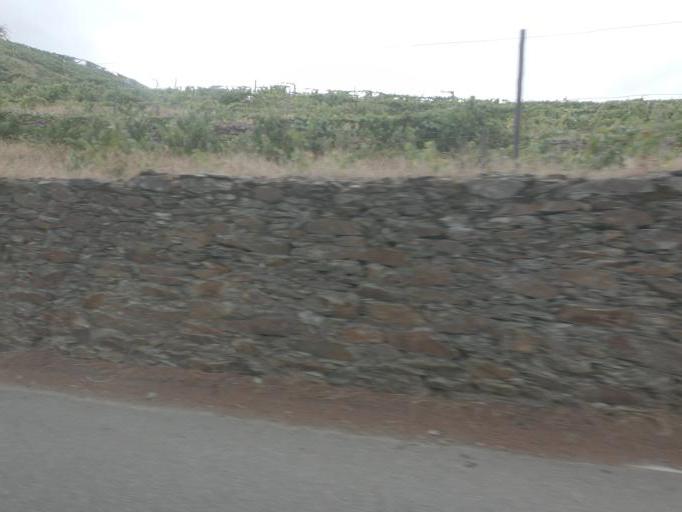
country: PT
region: Vila Real
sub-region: Sabrosa
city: Vilela
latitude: 41.2065
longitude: -7.5320
